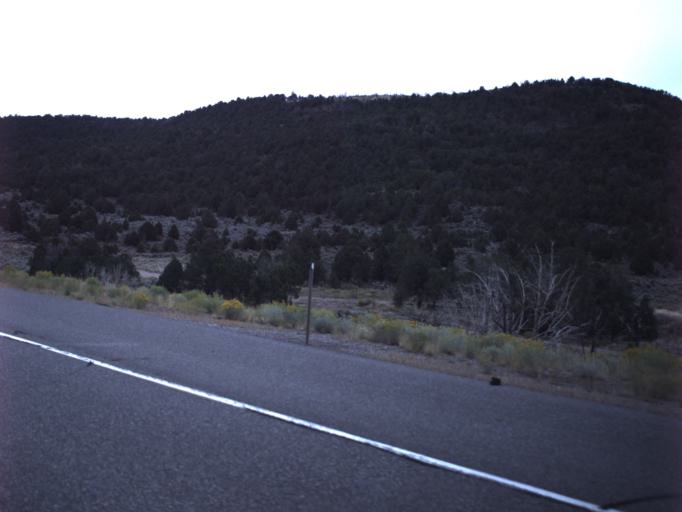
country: US
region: Utah
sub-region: Sevier County
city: Monroe
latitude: 38.5511
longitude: -112.4031
